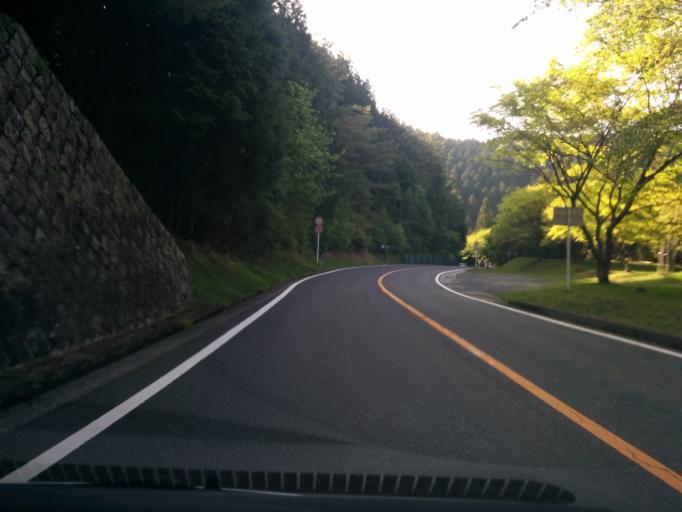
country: JP
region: Shiga Prefecture
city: Otsu-shi
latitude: 35.0893
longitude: 135.8388
